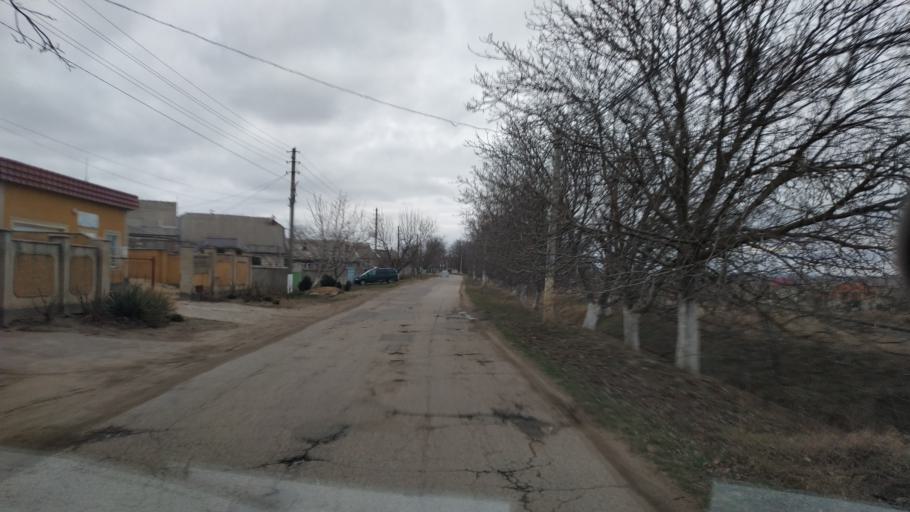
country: MD
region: Bender
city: Bender
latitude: 46.7719
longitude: 29.4826
